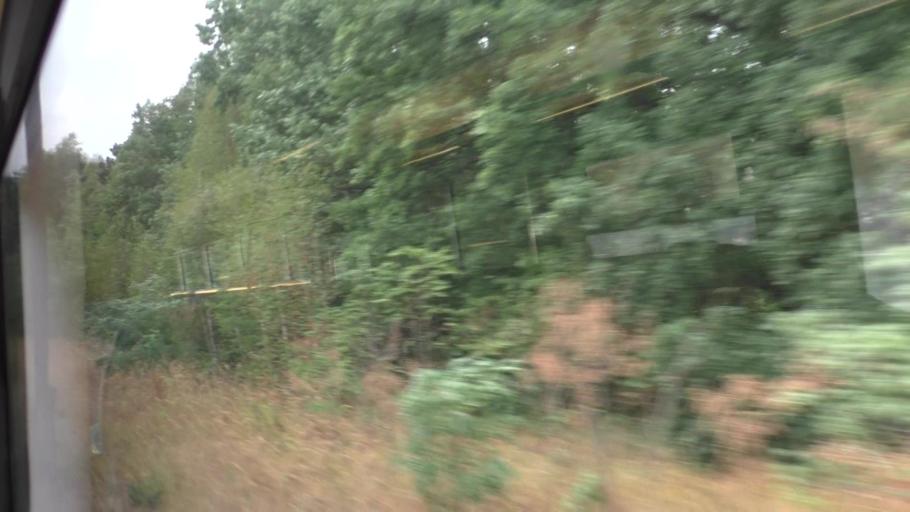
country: DE
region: Saxony
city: Goerlitz
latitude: 51.1309
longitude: 14.9733
